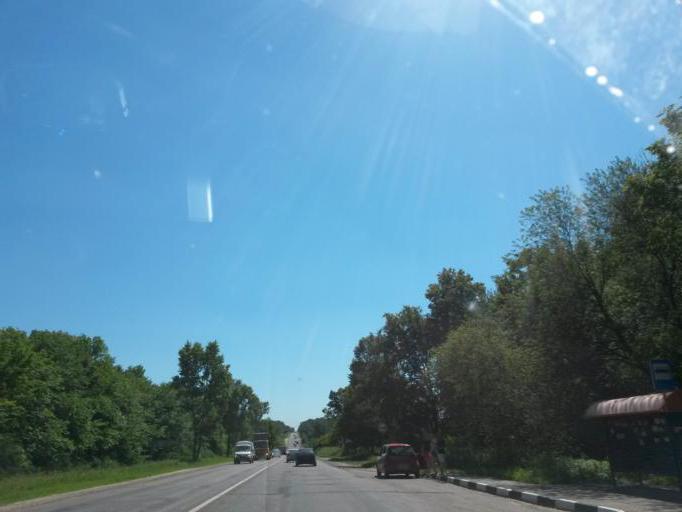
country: RU
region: Moskovskaya
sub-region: Chekhovskiy Rayon
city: Chekhov
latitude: 55.1024
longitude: 37.4450
